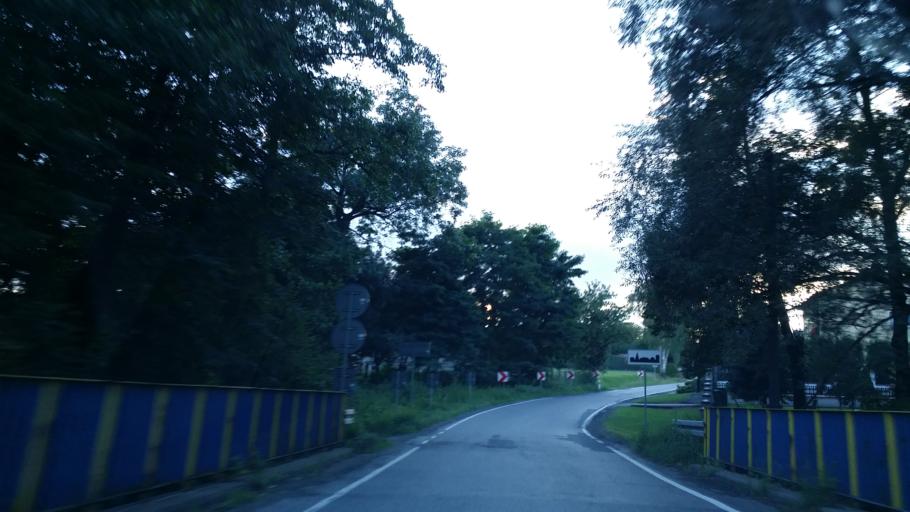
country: PL
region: Lesser Poland Voivodeship
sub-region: Powiat oswiecimski
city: Polanka Wielka
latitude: 49.9891
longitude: 19.3494
